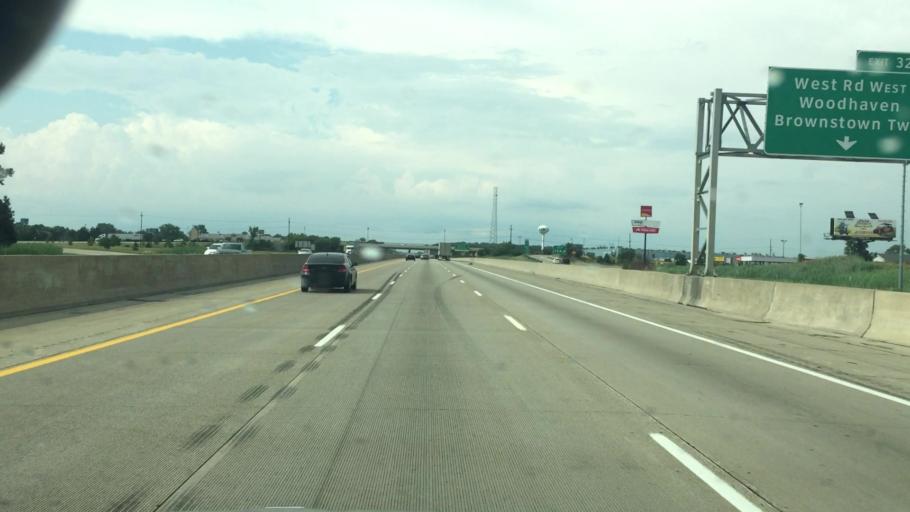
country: US
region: Michigan
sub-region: Wayne County
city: Woodhaven
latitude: 42.1345
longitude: -83.2414
